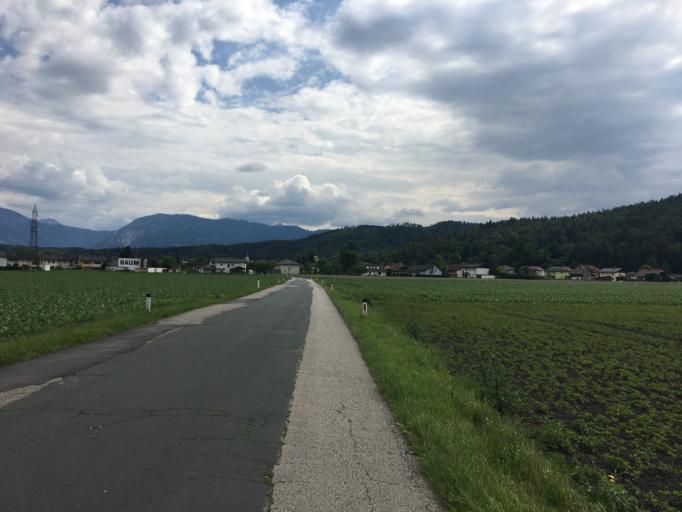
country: AT
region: Carinthia
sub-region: Klagenfurt am Woerthersee
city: Klagenfurt am Woerthersee
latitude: 46.6029
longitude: 14.2732
